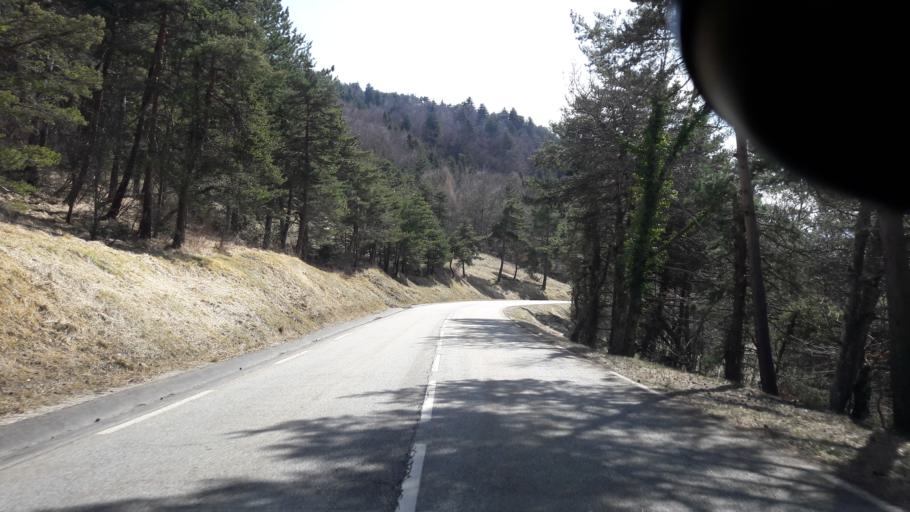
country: FR
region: Rhone-Alpes
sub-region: Departement de l'Isere
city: La Motte-Saint-Martin
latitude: 44.8967
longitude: 5.6345
